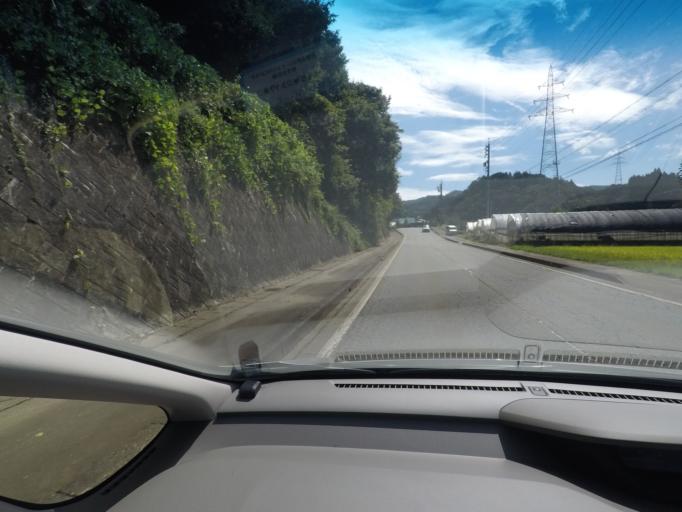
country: JP
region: Gifu
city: Takayama
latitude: 36.1398
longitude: 137.2851
